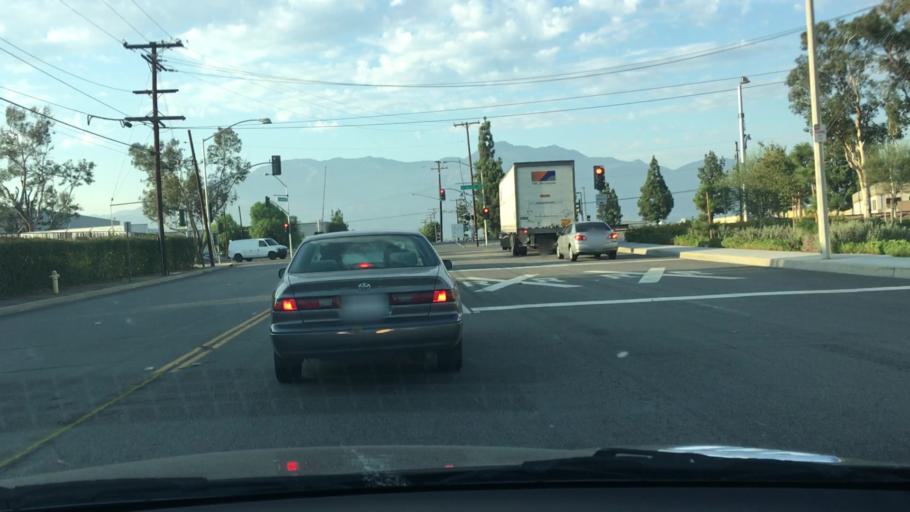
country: US
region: California
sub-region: San Bernardino County
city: Ontario
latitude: 34.0492
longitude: -117.6109
